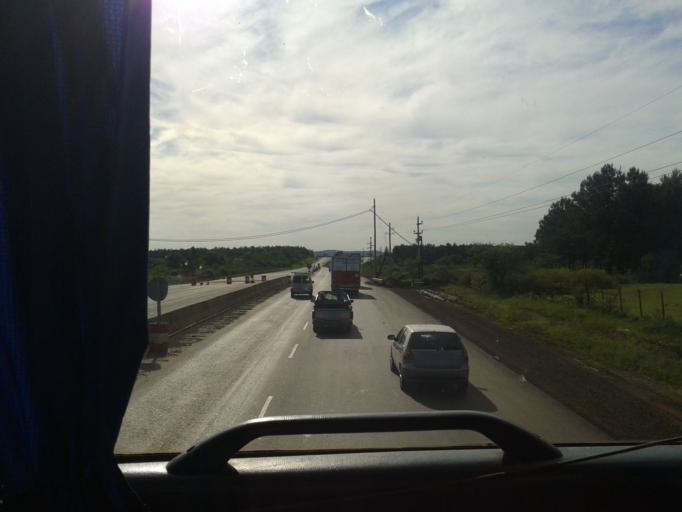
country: AR
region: Misiones
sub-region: Departamento de Candelaria
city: Candelaria
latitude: -27.4625
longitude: -55.6906
